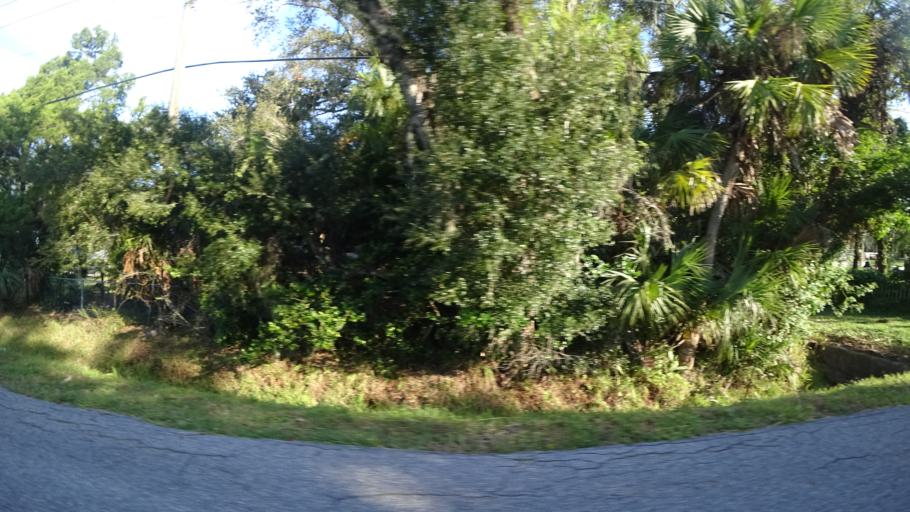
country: US
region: Florida
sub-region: Manatee County
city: Samoset
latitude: 27.4693
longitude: -82.5119
